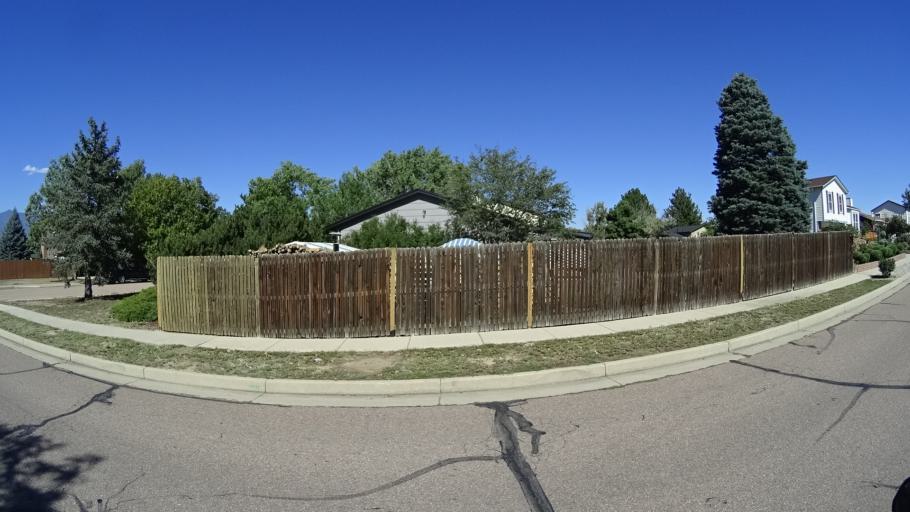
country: US
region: Colorado
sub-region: El Paso County
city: Cimarron Hills
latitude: 38.8192
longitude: -104.7301
